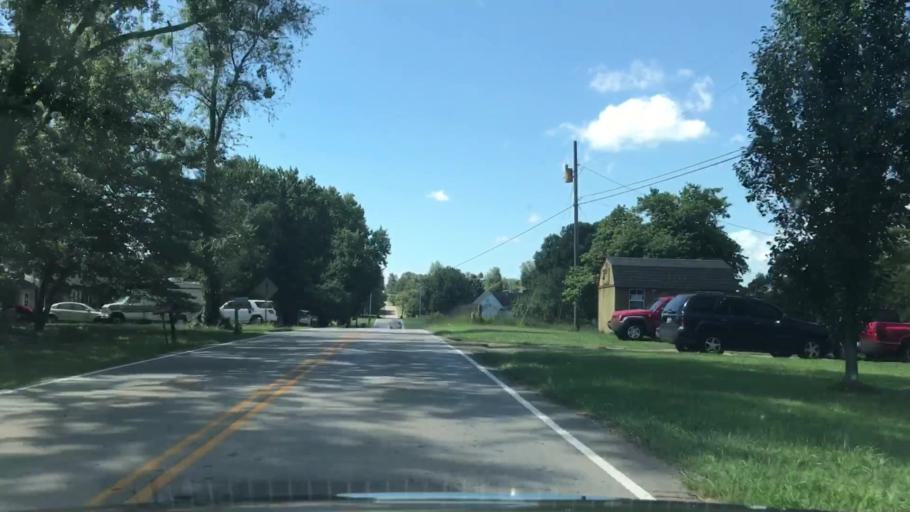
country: US
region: Kentucky
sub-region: Warren County
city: Plano
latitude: 36.9185
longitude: -86.4102
